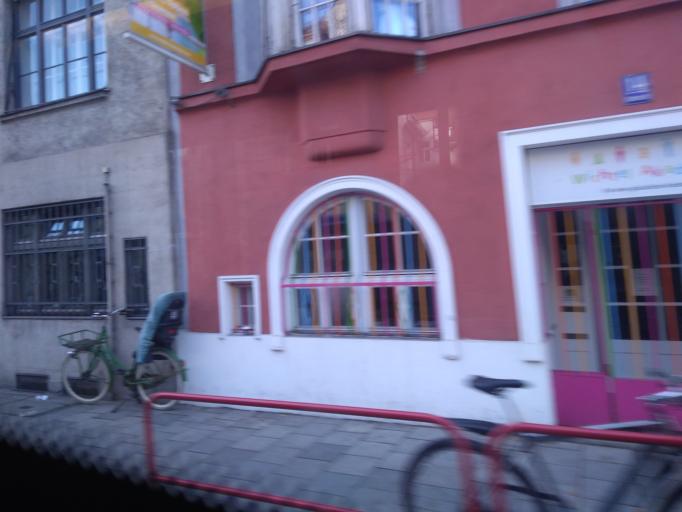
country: DE
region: Bavaria
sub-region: Upper Bavaria
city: Bogenhausen
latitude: 48.1661
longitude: 11.5912
